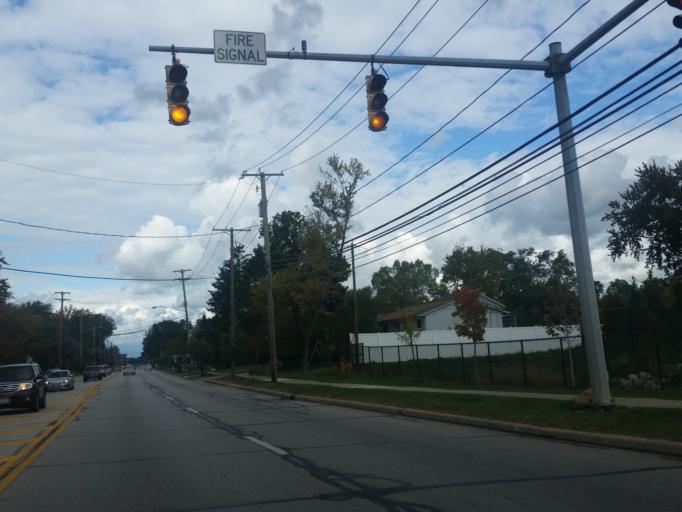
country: US
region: Ohio
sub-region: Cuyahoga County
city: Westlake
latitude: 41.4568
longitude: -81.9021
